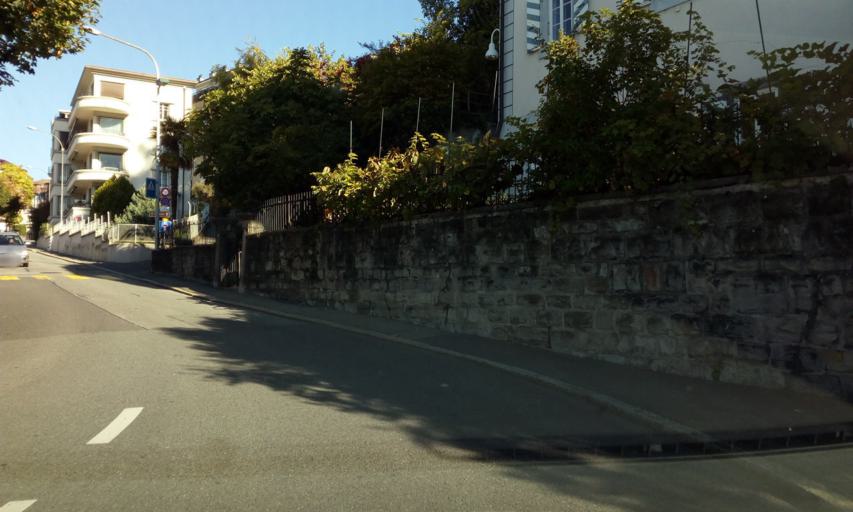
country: CH
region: Vaud
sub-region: Riviera-Pays-d'Enhaut District
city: Montreux
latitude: 46.4312
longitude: 6.9182
